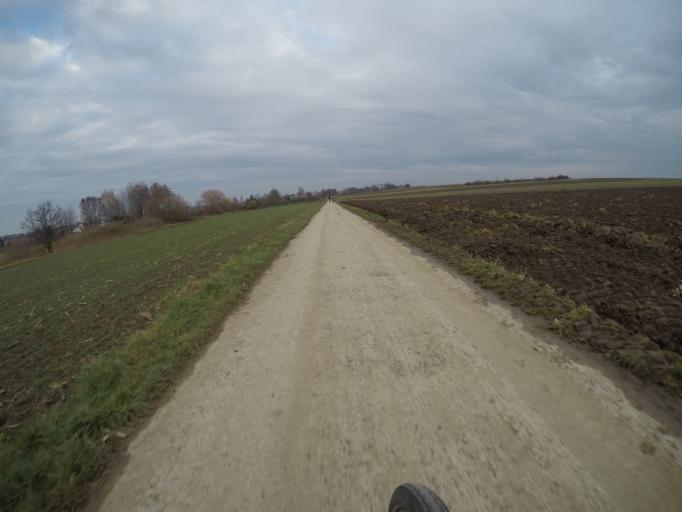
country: DE
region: Baden-Wuerttemberg
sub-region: Regierungsbezirk Stuttgart
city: Leinfelden-Echterdingen
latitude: 48.6961
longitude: 9.2045
